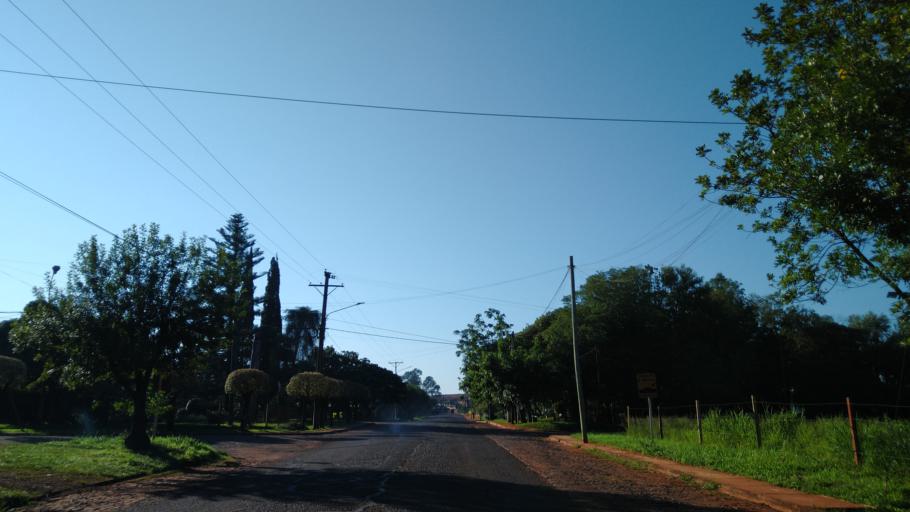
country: AR
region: Misiones
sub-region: Departamento de Montecarlo
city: Montecarlo
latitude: -26.5732
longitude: -54.7487
